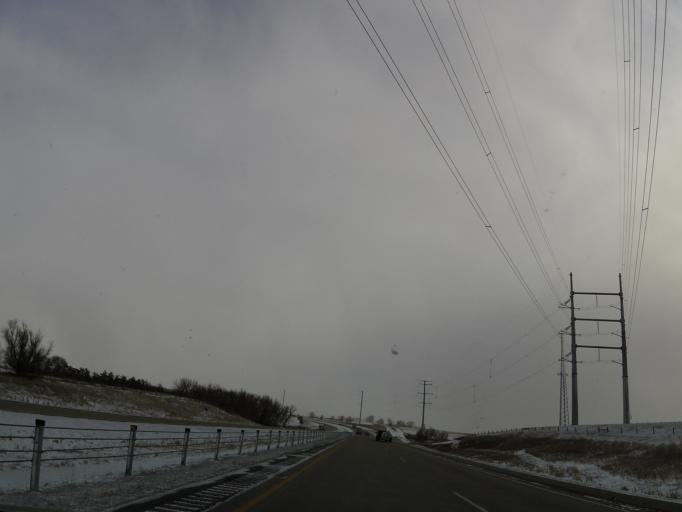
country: US
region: Minnesota
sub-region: Grant County
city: Elbow Lake
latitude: 46.0975
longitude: -95.8939
